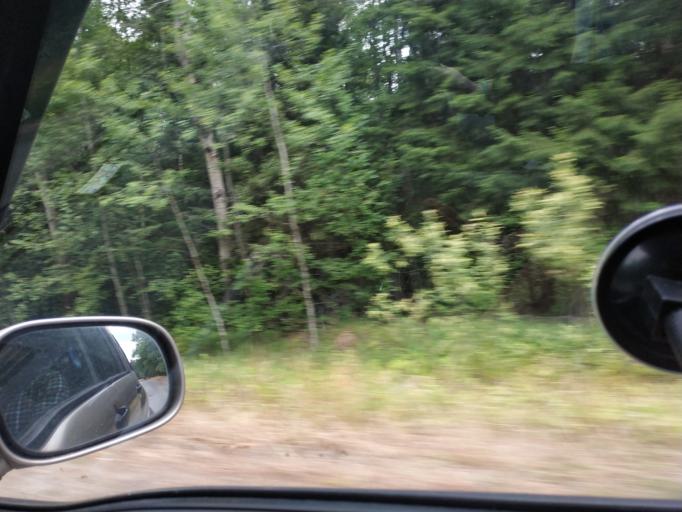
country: RU
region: Moskovskaya
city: Krasnoarmeysk
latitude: 56.0754
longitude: 38.2463
